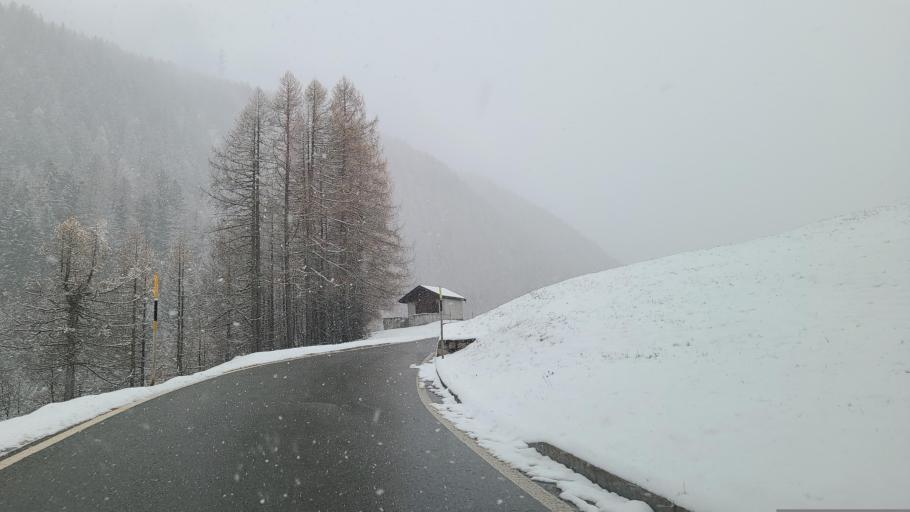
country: CH
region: Ticino
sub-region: Leventina District
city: Airolo
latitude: 46.5114
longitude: 8.5279
